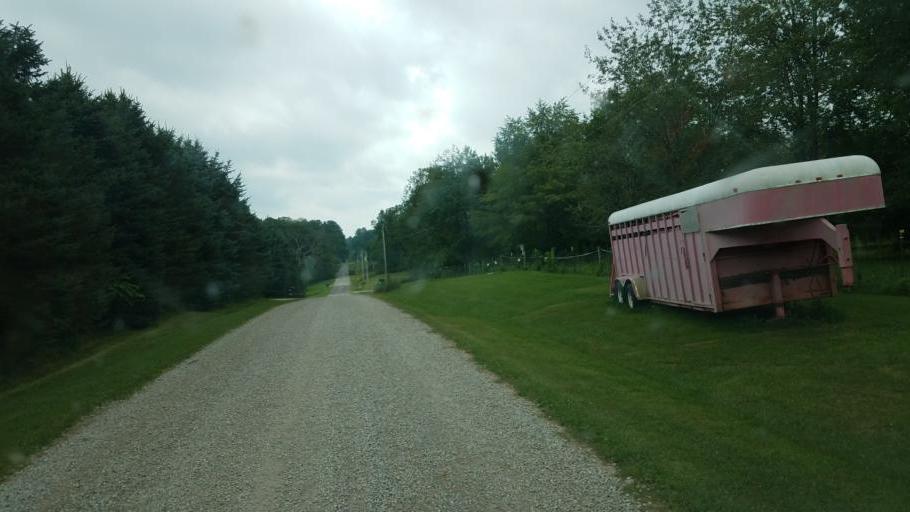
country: US
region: Ohio
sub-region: Morrow County
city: Mount Gilead
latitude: 40.5287
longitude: -82.7015
